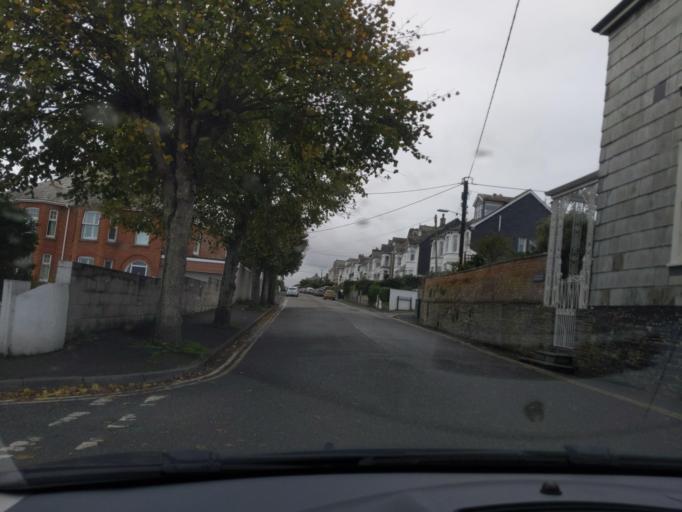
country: GB
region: England
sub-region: Cornwall
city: Padstow
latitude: 50.5390
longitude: -4.9381
